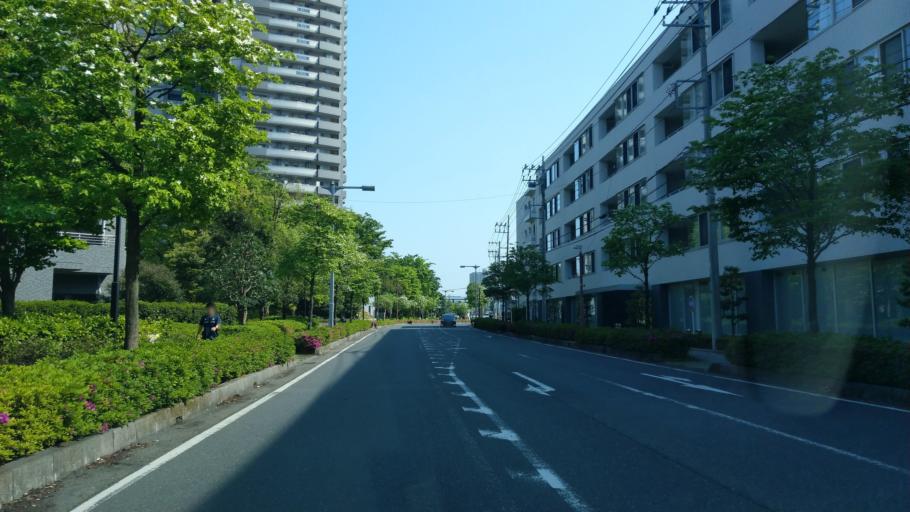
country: JP
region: Saitama
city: Kamifukuoka
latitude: 35.8623
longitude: 139.5183
